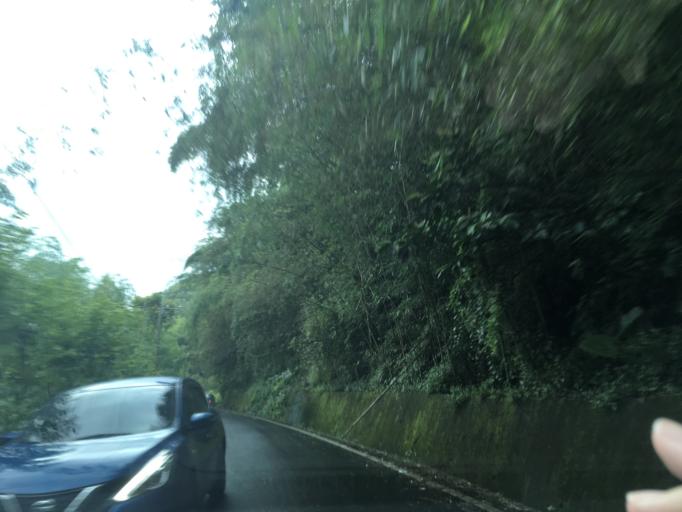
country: TW
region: Taiwan
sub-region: Chiayi
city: Jiayi Shi
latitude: 23.4427
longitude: 120.6698
